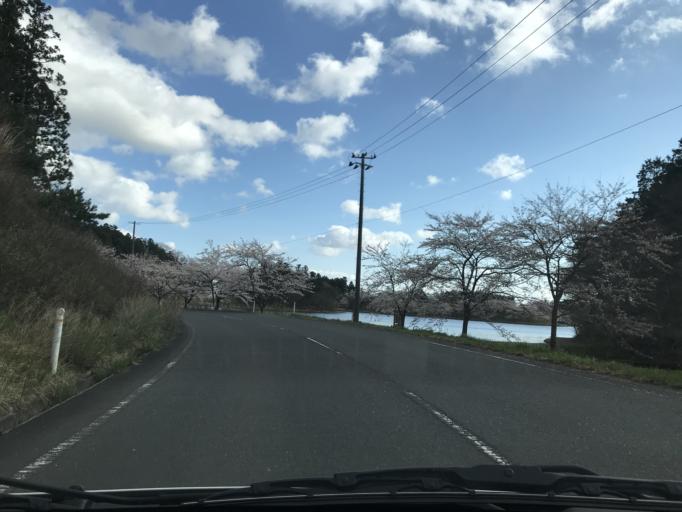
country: JP
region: Miyagi
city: Wakuya
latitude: 38.6134
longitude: 141.2399
